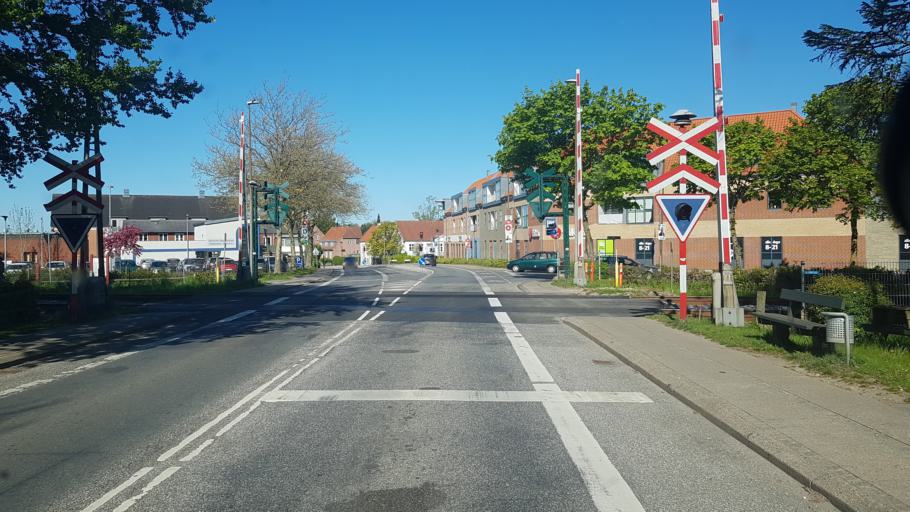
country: DK
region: South Denmark
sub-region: Faaborg-Midtfyn Kommune
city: Ringe
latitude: 55.2357
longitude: 10.4808
